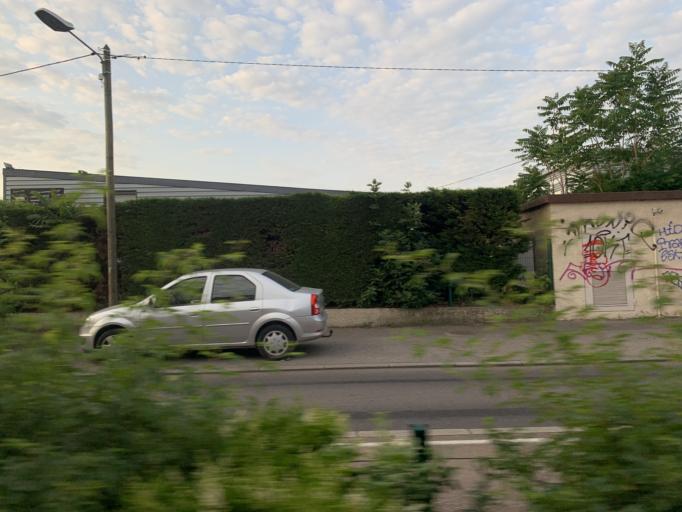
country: FR
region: Rhone-Alpes
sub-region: Departement du Rhone
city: Villeurbanne
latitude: 45.7578
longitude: 4.9063
